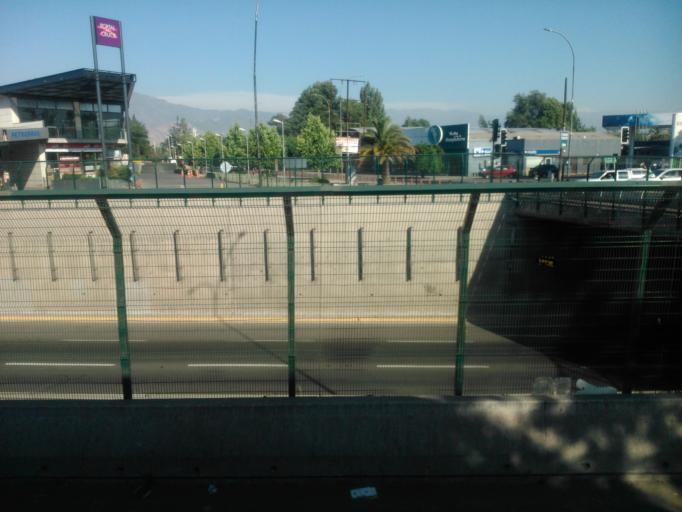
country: CL
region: Santiago Metropolitan
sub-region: Provincia de Maipo
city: Buin
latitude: -33.7330
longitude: -70.7339
